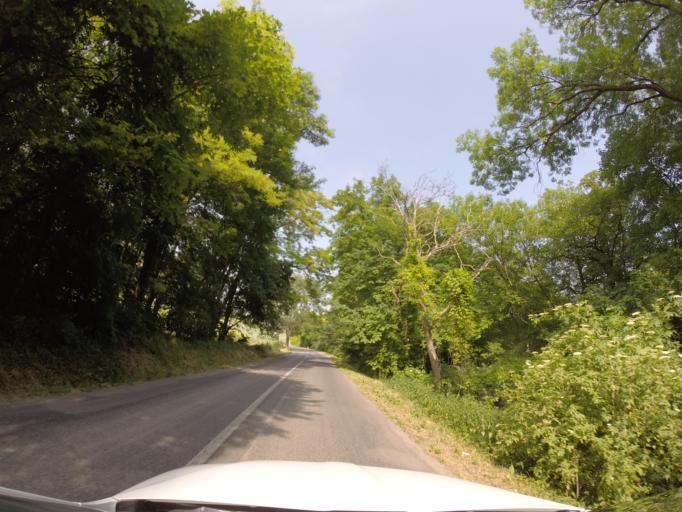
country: CZ
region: South Moravian
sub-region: Okres Breclav
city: Mikulov
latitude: 48.8601
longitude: 16.6491
